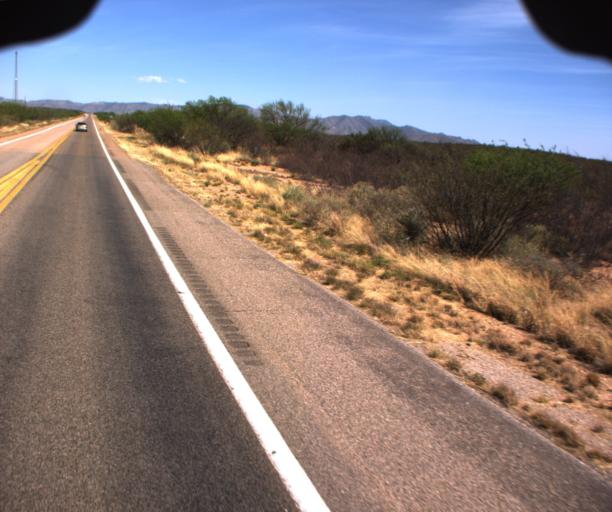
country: US
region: Arizona
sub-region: Cochise County
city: Sierra Vista Southeast
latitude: 31.5510
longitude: -110.1147
